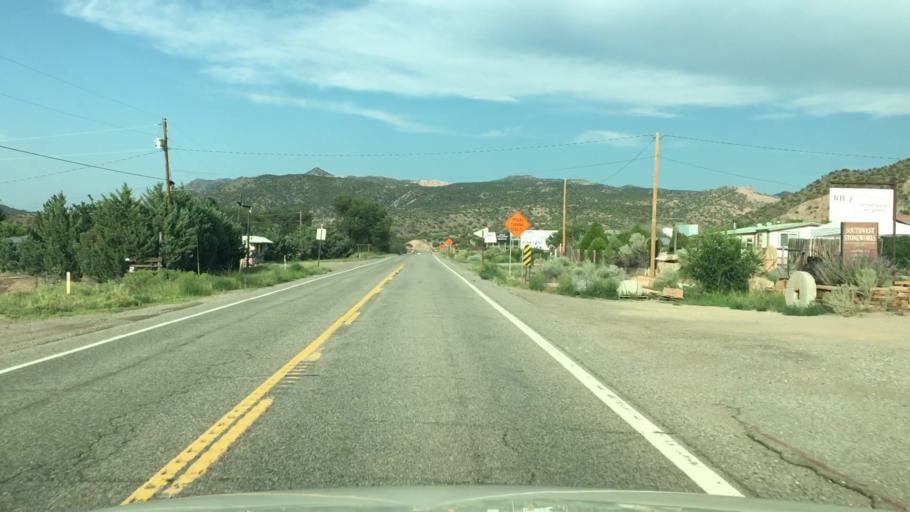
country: US
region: New Mexico
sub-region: Rio Arriba County
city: Chimayo
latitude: 36.2168
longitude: -105.8781
